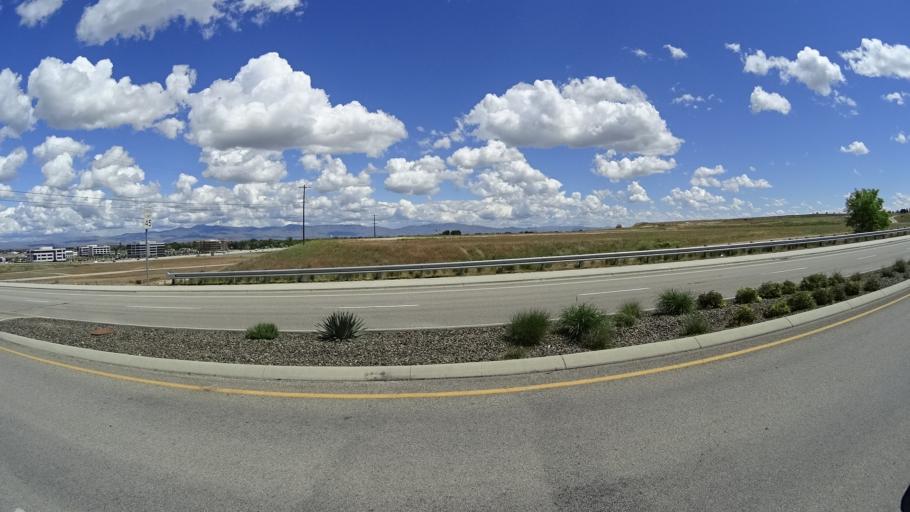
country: US
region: Idaho
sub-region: Ada County
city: Meridian
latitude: 43.5898
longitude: -116.4339
